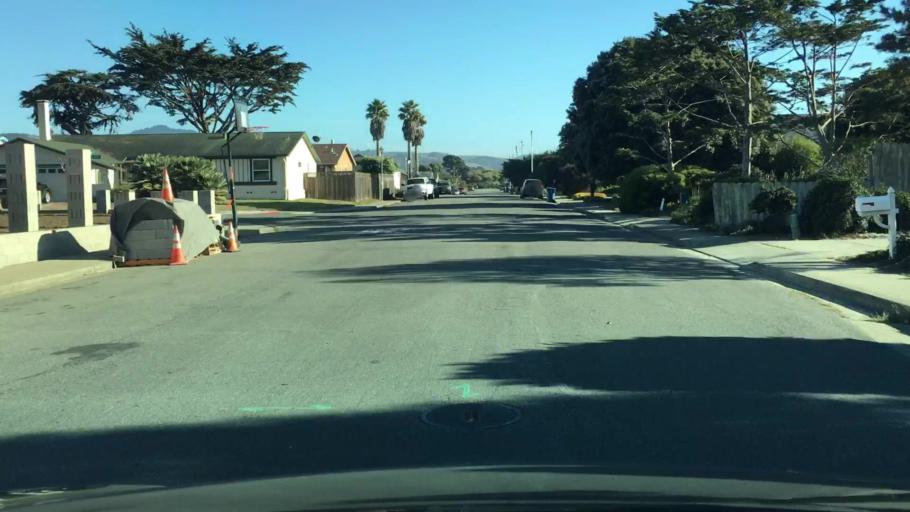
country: US
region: California
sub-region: San Mateo County
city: Half Moon Bay
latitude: 37.4768
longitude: -122.4459
